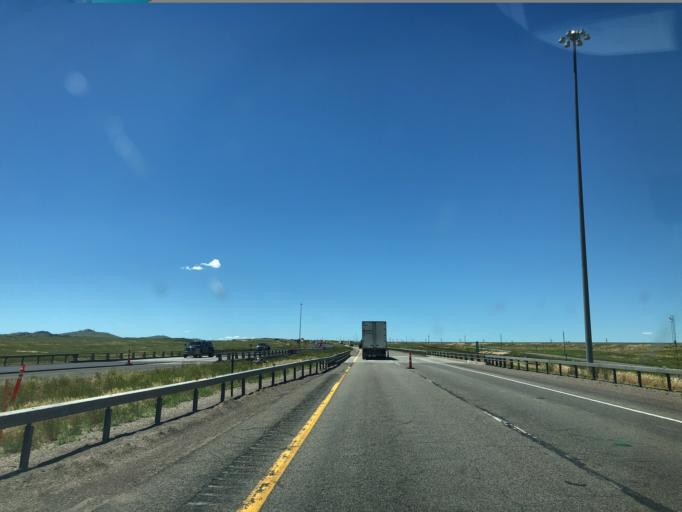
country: US
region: Wyoming
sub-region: Laramie County
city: Cheyenne
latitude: 41.0983
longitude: -105.1150
